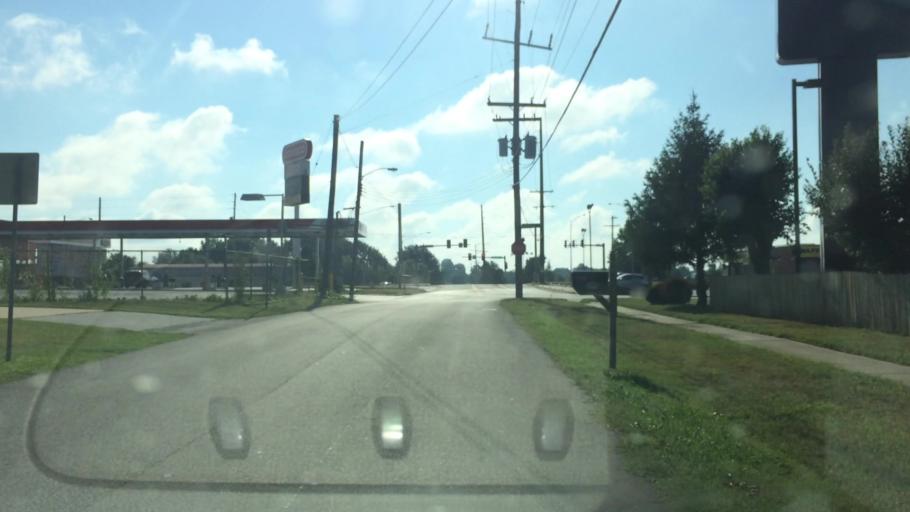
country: US
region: Missouri
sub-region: Greene County
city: Springfield
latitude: 37.2542
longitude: -93.2665
